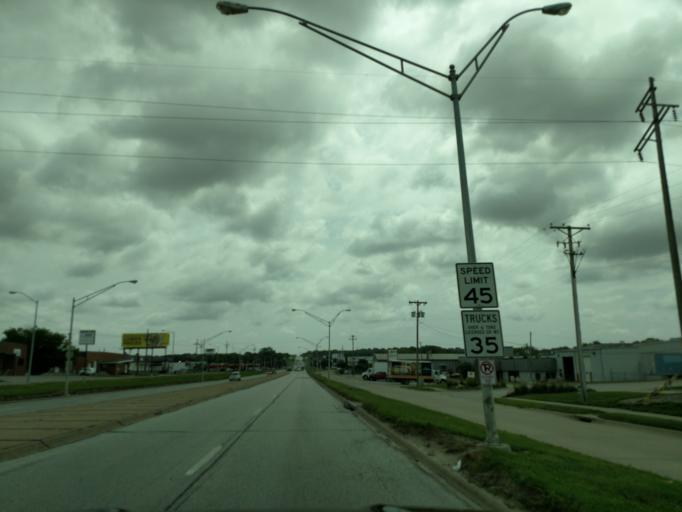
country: US
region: Nebraska
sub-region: Douglas County
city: Ralston
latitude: 41.2124
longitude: -96.0194
